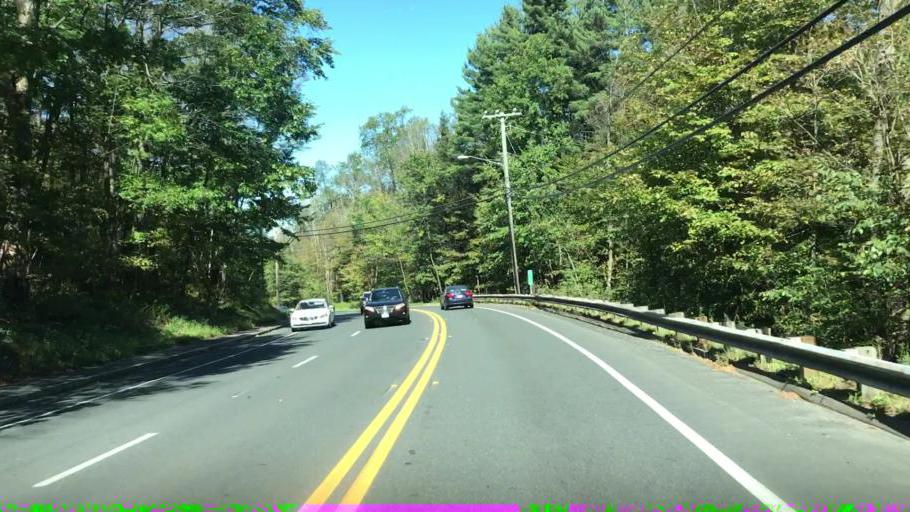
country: US
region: Massachusetts
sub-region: Berkshire County
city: Pittsfield
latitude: 42.4189
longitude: -73.2604
